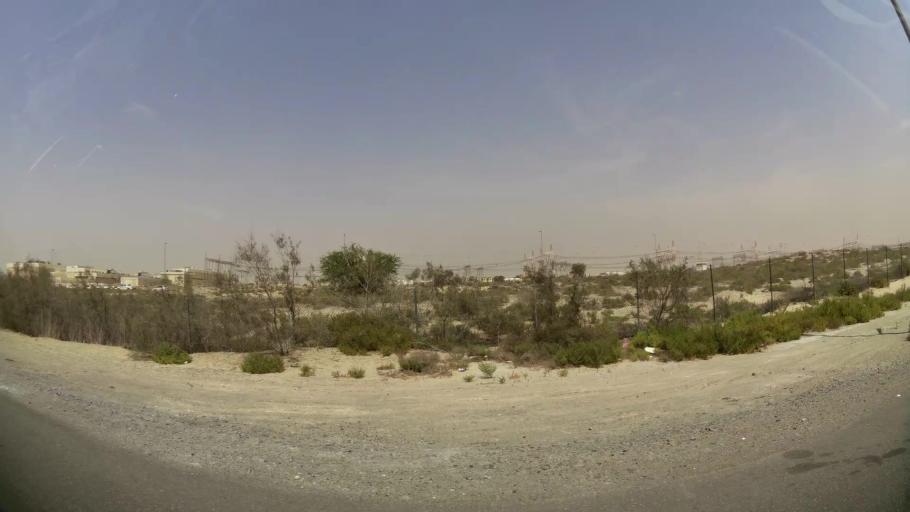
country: AE
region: Ash Shariqah
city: Sharjah
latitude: 25.2305
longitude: 55.4047
